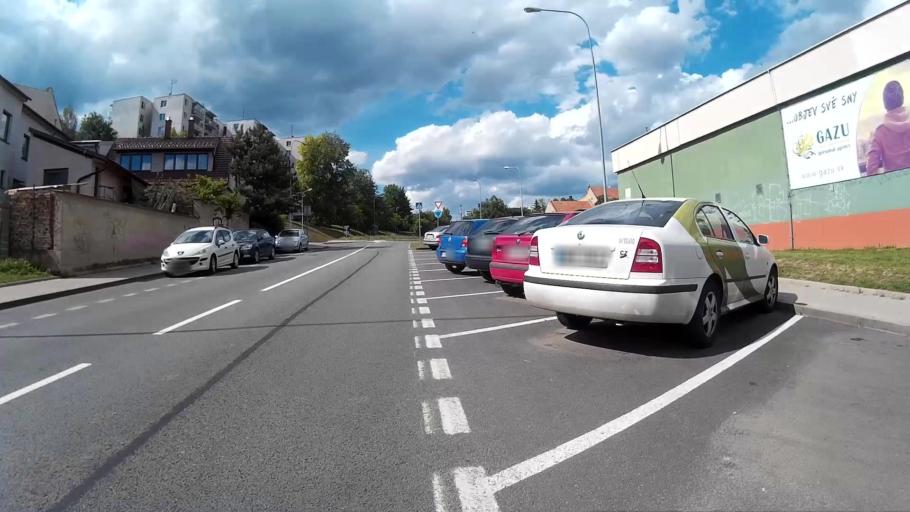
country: CZ
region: South Moravian
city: Moravany
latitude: 49.1677
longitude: 16.5754
